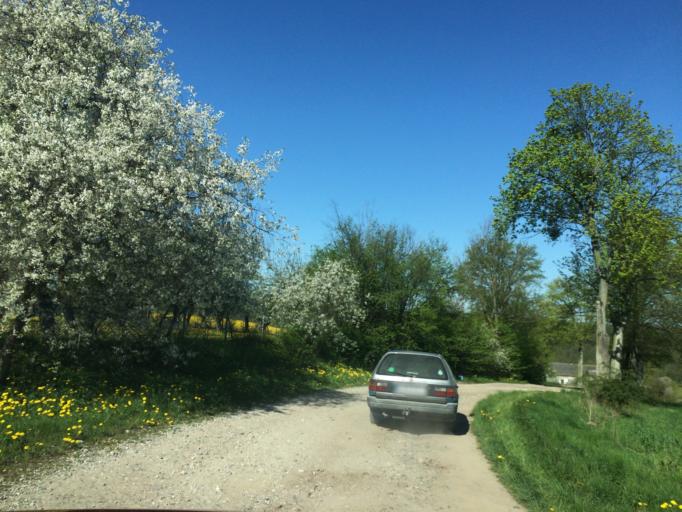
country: PL
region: Warmian-Masurian Voivodeship
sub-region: Powiat nowomiejski
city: Biskupiec
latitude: 53.4870
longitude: 19.4791
